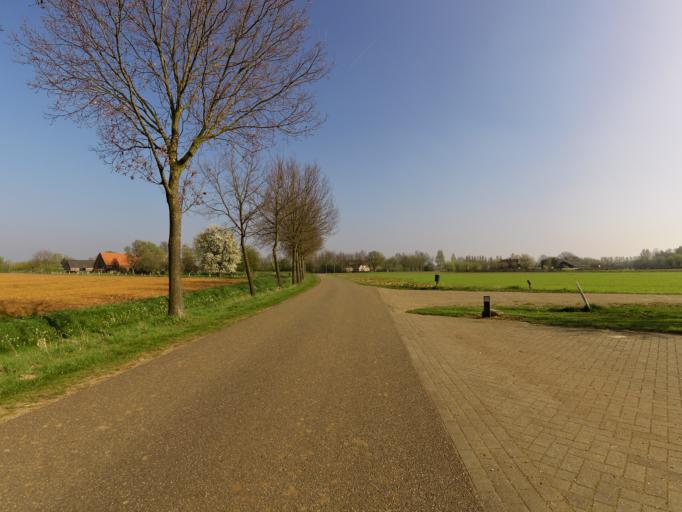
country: NL
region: Gelderland
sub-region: Gemeente Bronckhorst
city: Hengelo
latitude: 52.0304
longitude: 6.2697
